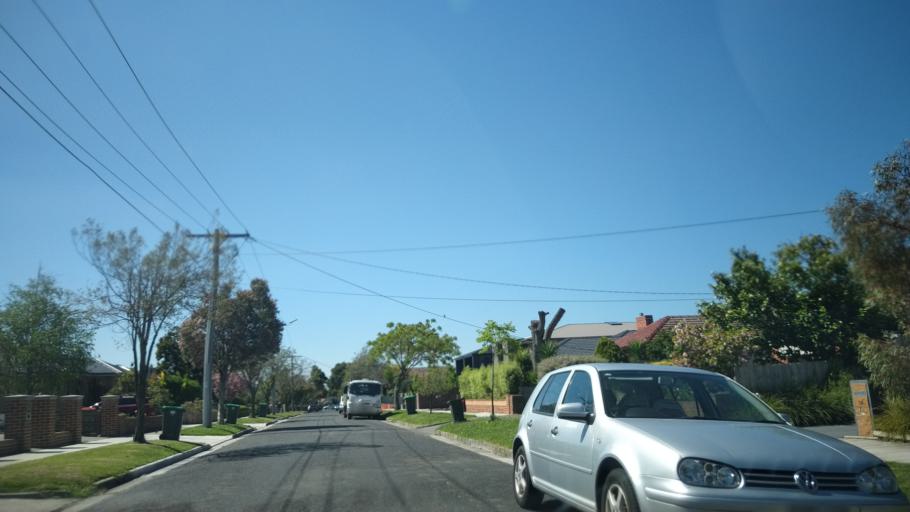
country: AU
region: Victoria
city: Hughesdale
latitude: -37.9111
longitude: 145.0767
